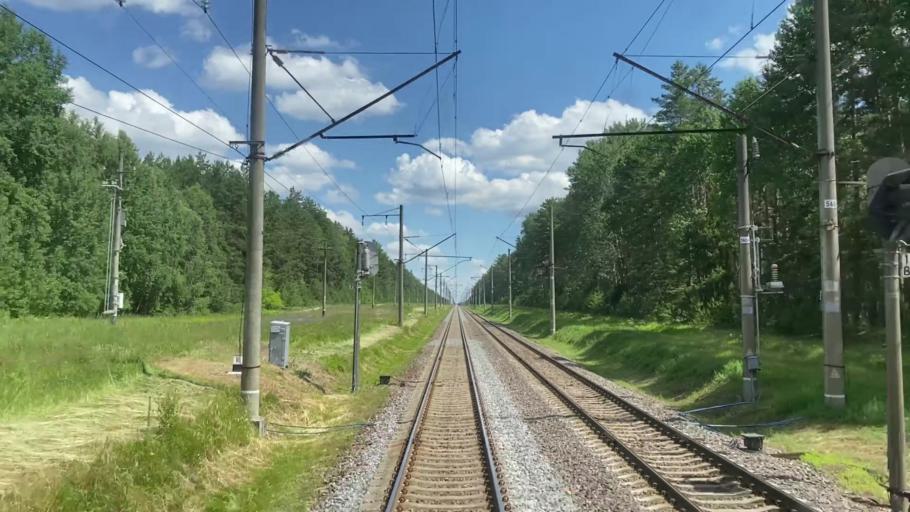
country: BY
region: Grodnenskaya
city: Zhyrovichy
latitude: 52.8594
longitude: 25.5855
